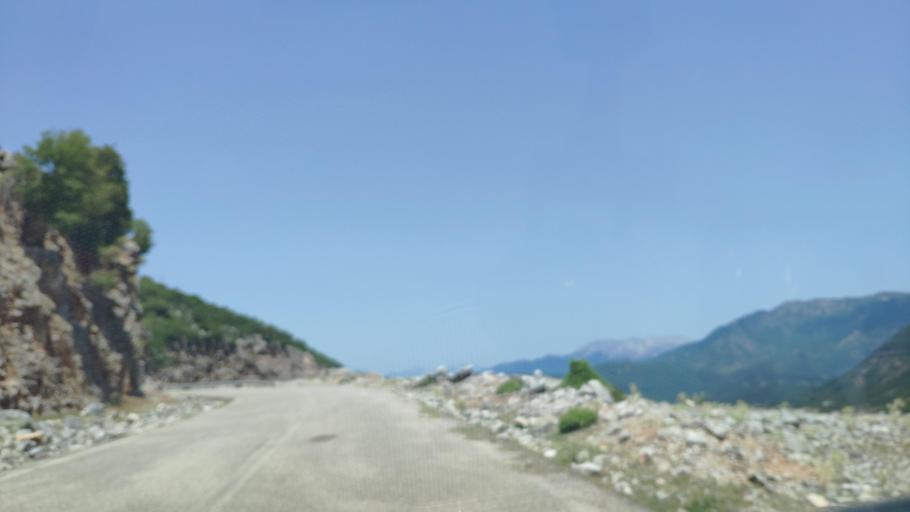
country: GR
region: Thessaly
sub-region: Nomos Kardhitsas
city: Anthiro
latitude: 39.1211
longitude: 21.4019
